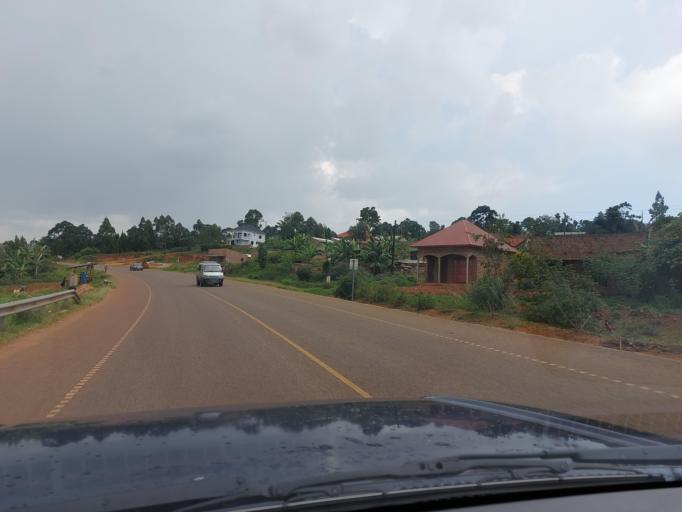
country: UG
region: Central Region
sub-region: Buikwe District
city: Buikwe
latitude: 0.2386
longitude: 32.9266
